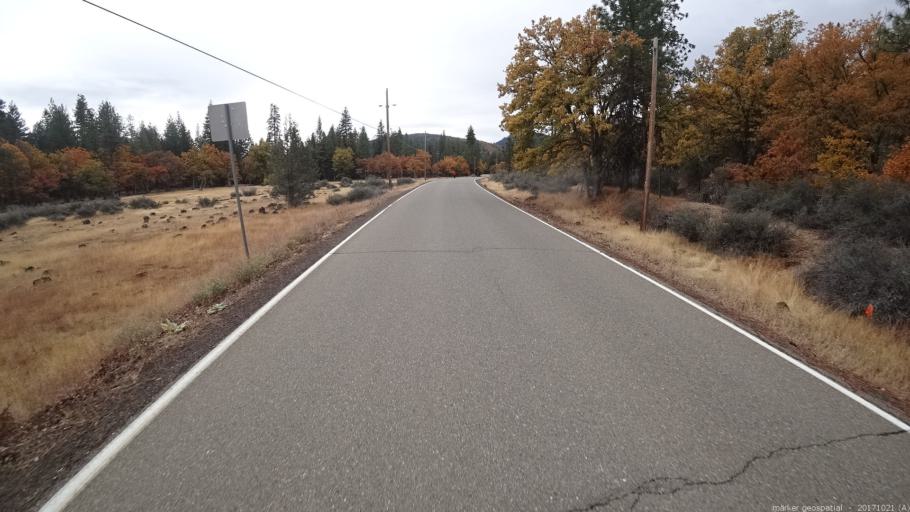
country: US
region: California
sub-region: Shasta County
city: Burney
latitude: 41.0339
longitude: -121.6715
